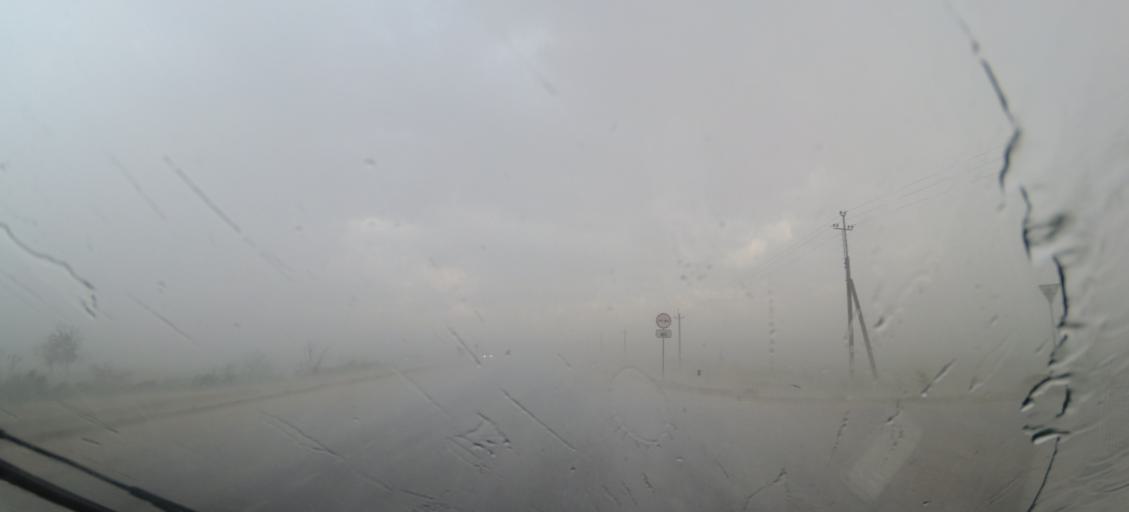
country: RU
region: Rostov
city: Proletarsk
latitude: 46.6903
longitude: 41.7364
